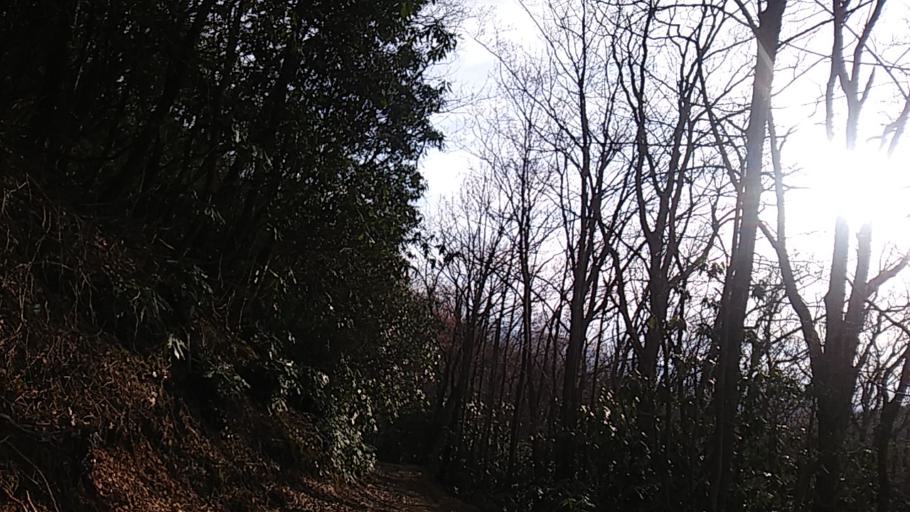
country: US
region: Tennessee
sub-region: Greene County
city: Tusculum
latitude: 36.0659
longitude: -82.6773
